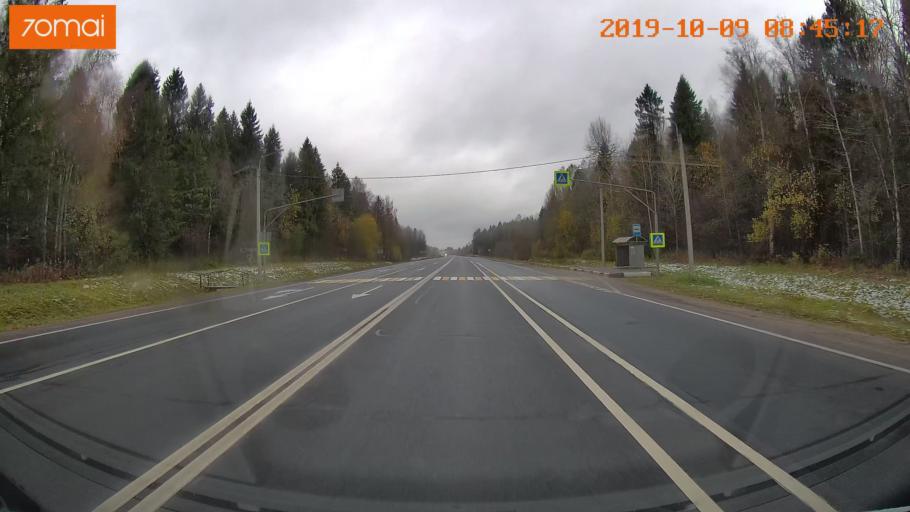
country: RU
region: Vologda
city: Gryazovets
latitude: 59.0465
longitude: 40.0937
